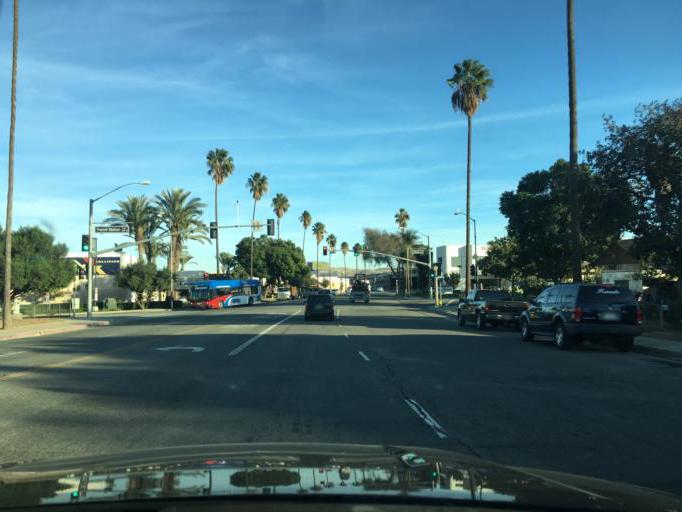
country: US
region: California
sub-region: Riverside County
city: Corona
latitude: 33.8814
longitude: -117.5639
